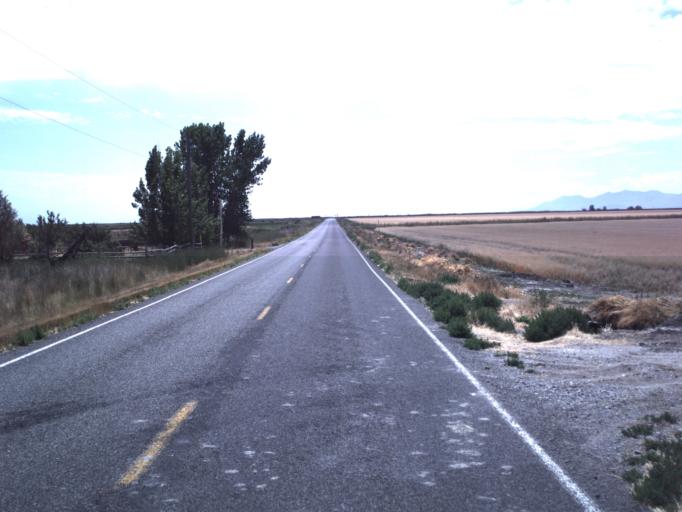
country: US
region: Utah
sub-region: Box Elder County
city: Tremonton
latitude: 41.6457
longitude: -112.3142
